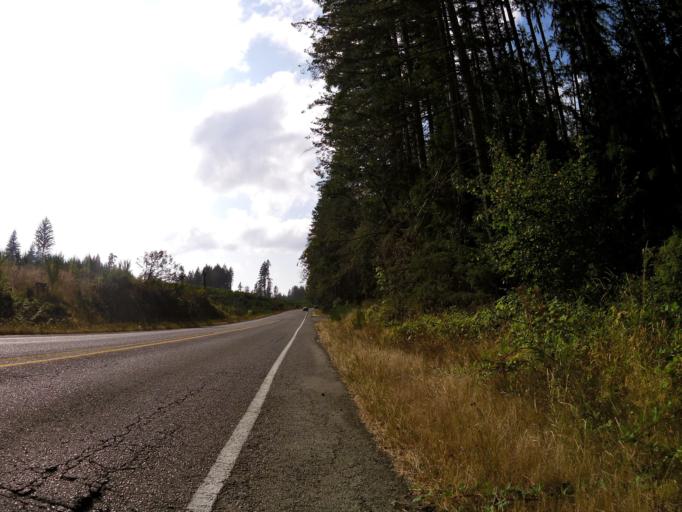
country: US
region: Washington
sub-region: Kitsap County
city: Erlands Point-Kitsap Lake
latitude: 47.5246
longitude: -122.7568
